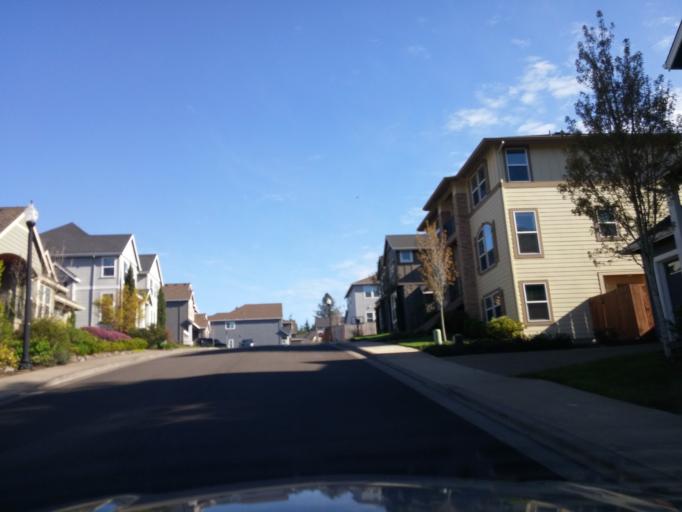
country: US
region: Oregon
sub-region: Washington County
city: Cedar Mill
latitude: 45.5335
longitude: -122.7941
